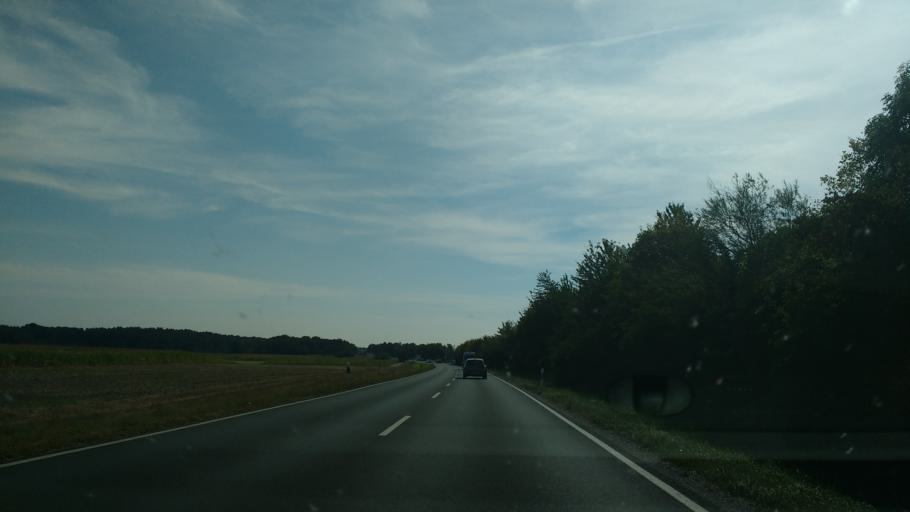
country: DE
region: Bavaria
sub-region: Regierungsbezirk Mittelfranken
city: Hessdorf
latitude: 49.6298
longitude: 10.9075
